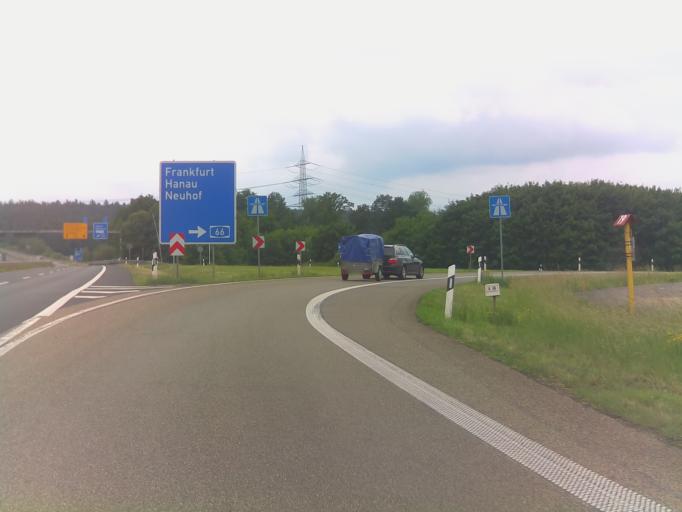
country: DE
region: Hesse
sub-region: Regierungsbezirk Kassel
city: Eichenzell
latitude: 50.4897
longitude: 9.6859
